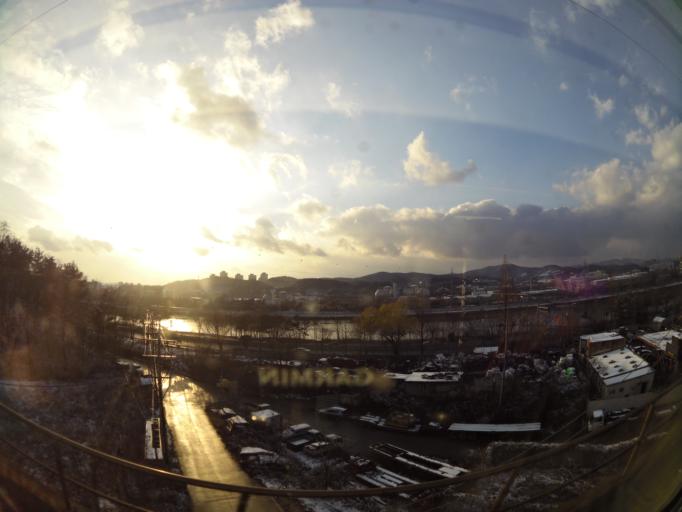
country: KR
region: Daejeon
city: Songgang-dong
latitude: 36.3857
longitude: 127.4138
